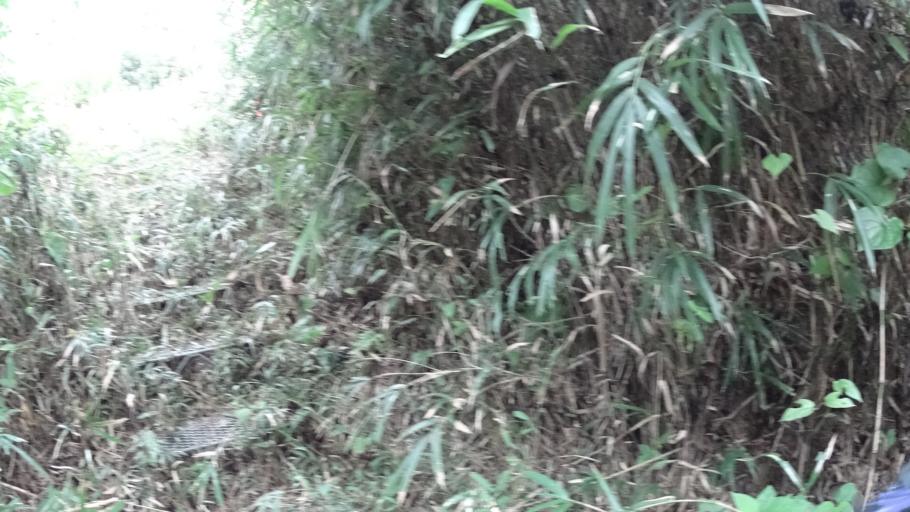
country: JP
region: Kanagawa
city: Yokosuka
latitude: 35.2897
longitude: 139.6228
